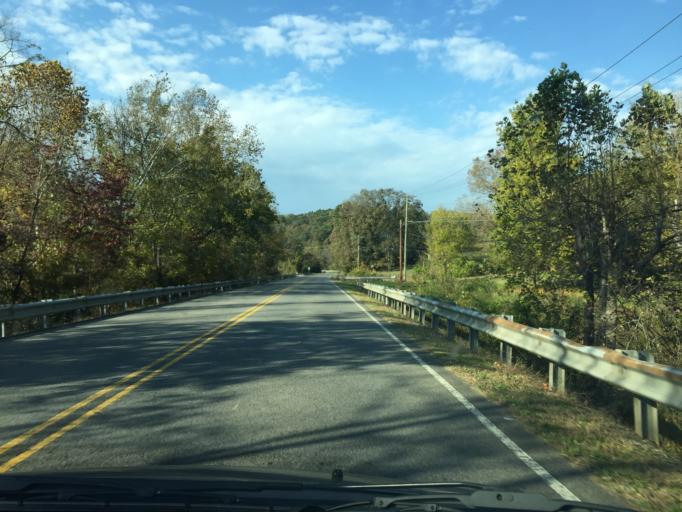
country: US
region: Tennessee
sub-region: Loudon County
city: Loudon
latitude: 35.7032
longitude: -84.3433
